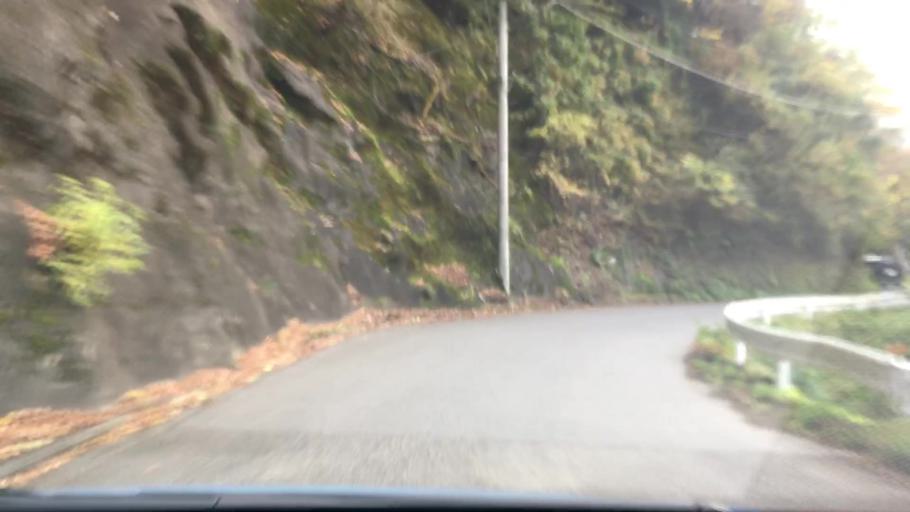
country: JP
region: Yamanashi
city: Uenohara
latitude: 35.5592
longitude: 139.1623
